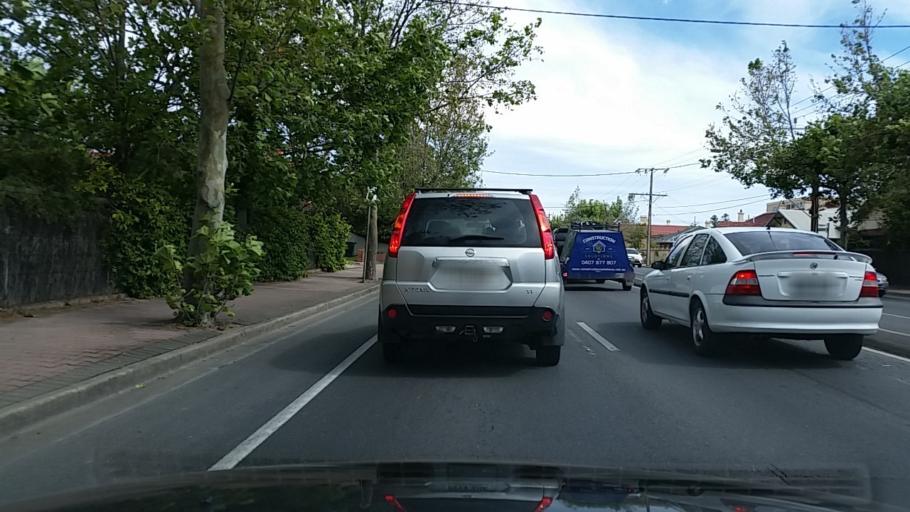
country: AU
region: South Australia
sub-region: Adelaide
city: Glenelg
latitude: -34.9808
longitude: 138.5203
